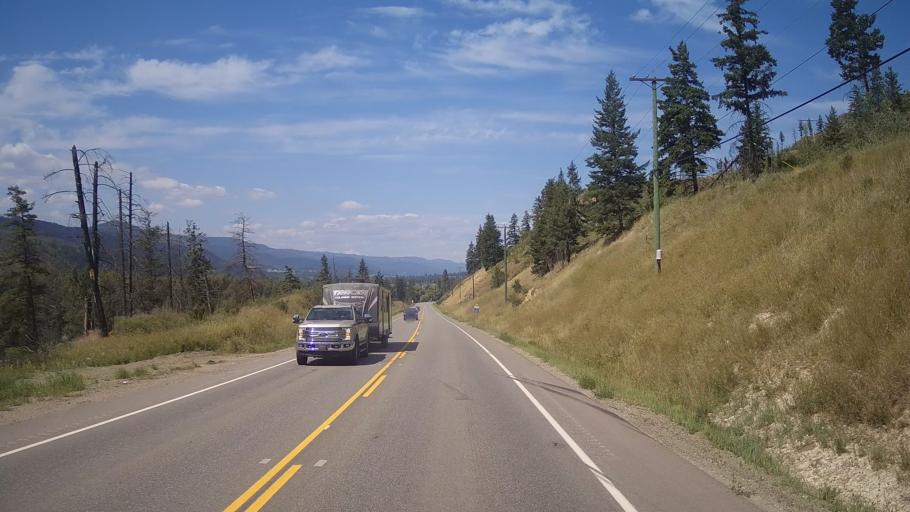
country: CA
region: British Columbia
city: Kamloops
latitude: 51.1513
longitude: -120.1174
